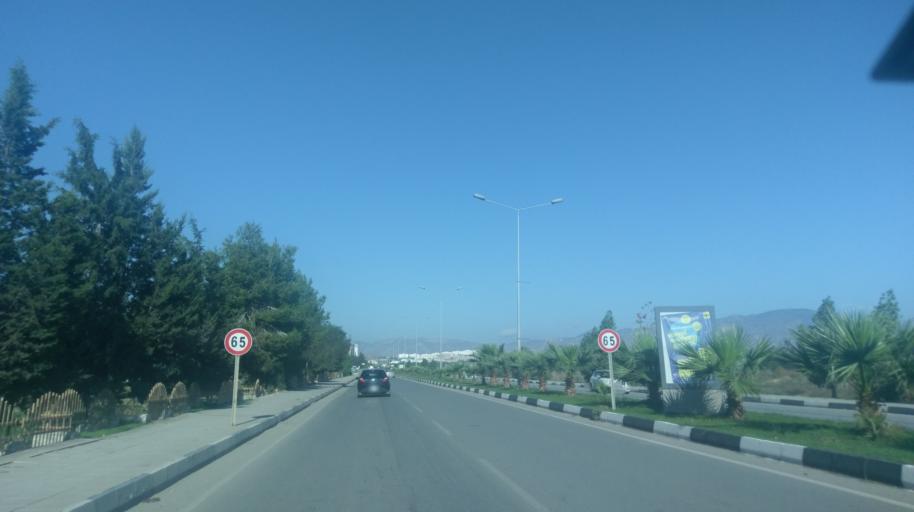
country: CY
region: Lefkosia
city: Nicosia
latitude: 35.2147
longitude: 33.3340
